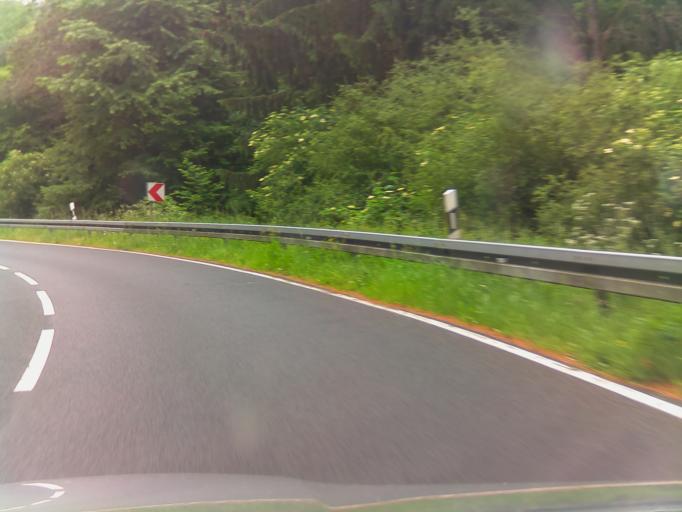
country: DE
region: Bavaria
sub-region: Regierungsbezirk Unterfranken
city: Schondra
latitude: 50.2388
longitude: 9.8241
